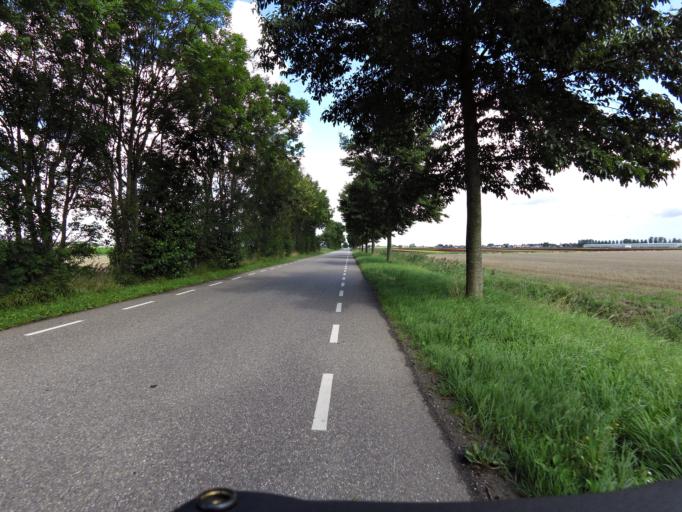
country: NL
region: North Brabant
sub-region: Gemeente Steenbergen
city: Nieuw-Vossemeer
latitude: 51.6767
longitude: 4.2671
